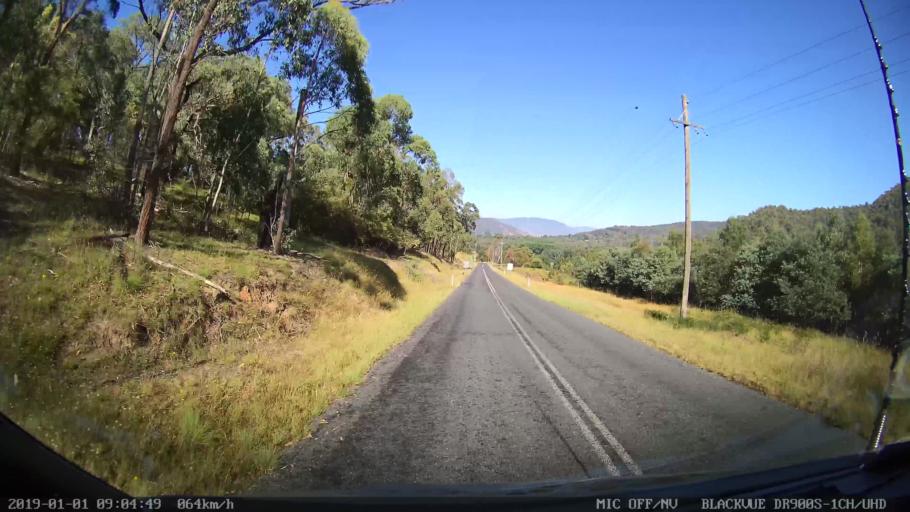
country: AU
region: New South Wales
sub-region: Snowy River
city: Jindabyne
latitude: -36.2212
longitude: 148.1522
